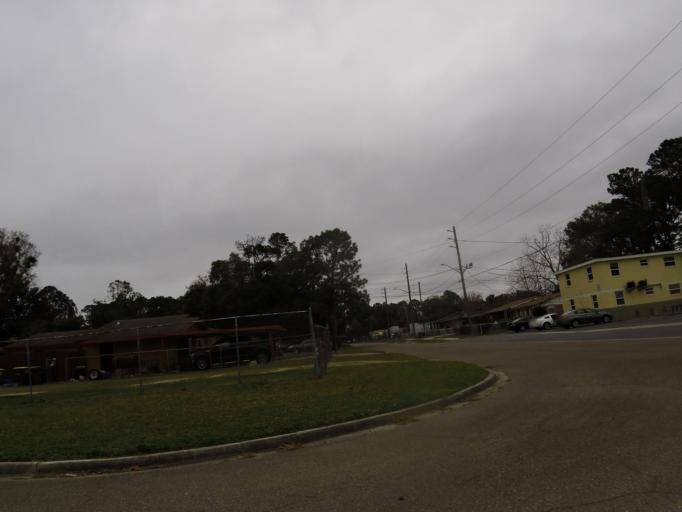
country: US
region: Florida
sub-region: Duval County
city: Jacksonville
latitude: 30.3611
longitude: -81.6989
